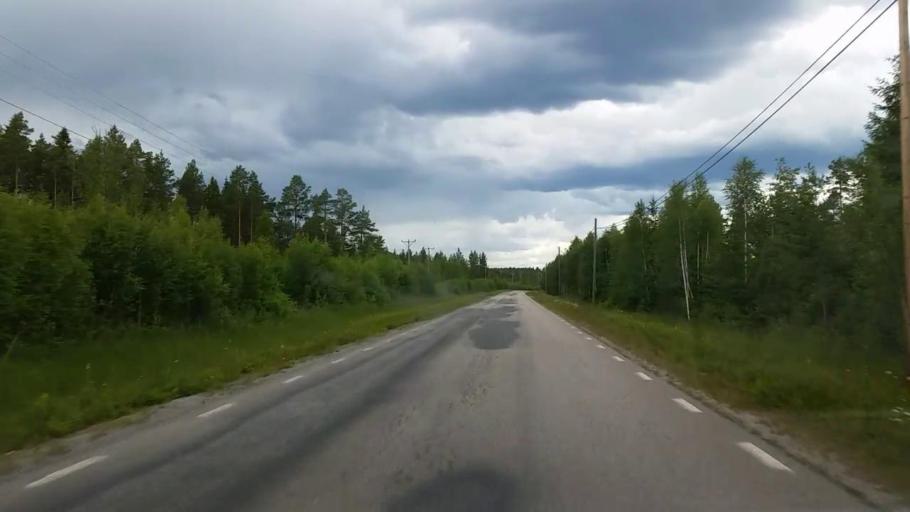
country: SE
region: Gaevleborg
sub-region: Ovanakers Kommun
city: Edsbyn
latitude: 61.4492
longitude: 15.8818
